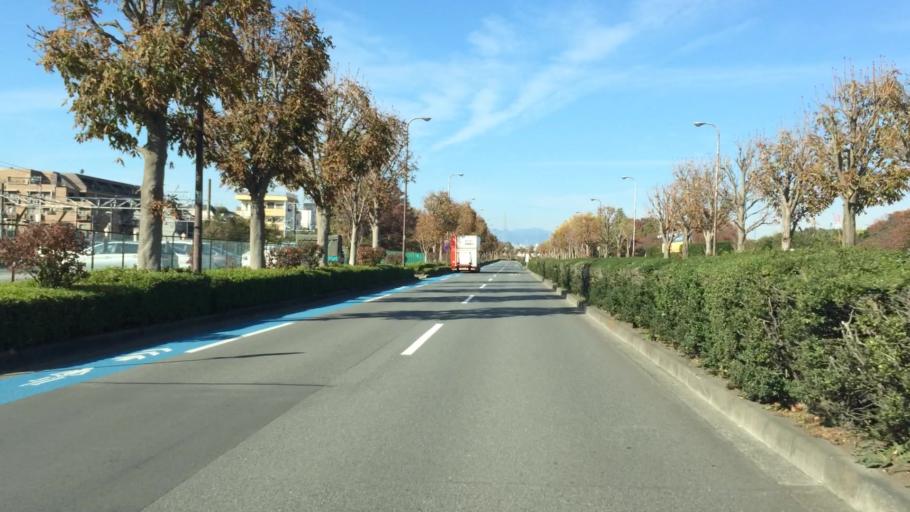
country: JP
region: Tokyo
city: Hino
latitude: 35.7040
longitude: 139.3935
